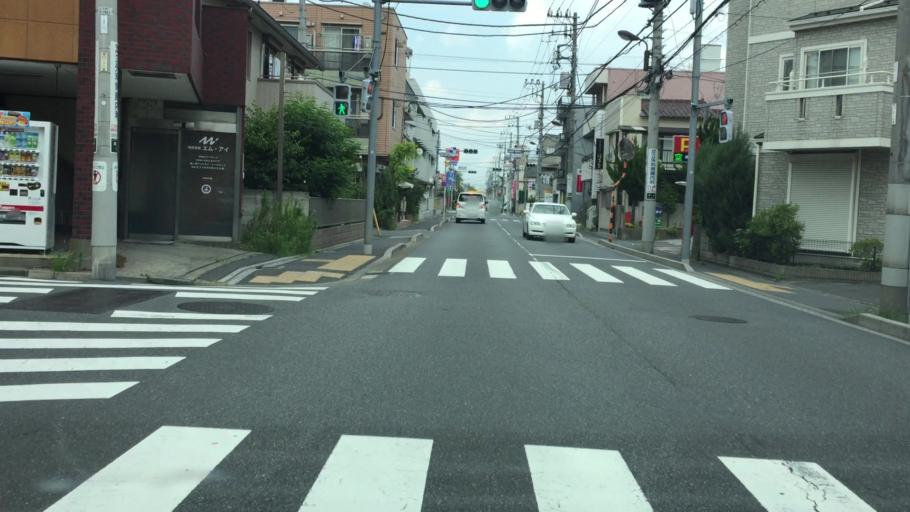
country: JP
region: Saitama
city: Soka
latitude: 35.7729
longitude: 139.8129
